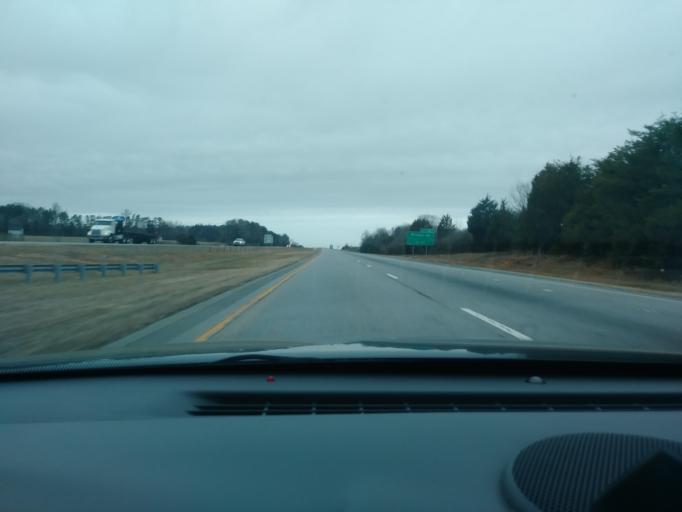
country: US
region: North Carolina
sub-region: Yadkin County
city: Jonesville
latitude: 36.1241
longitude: -80.8209
